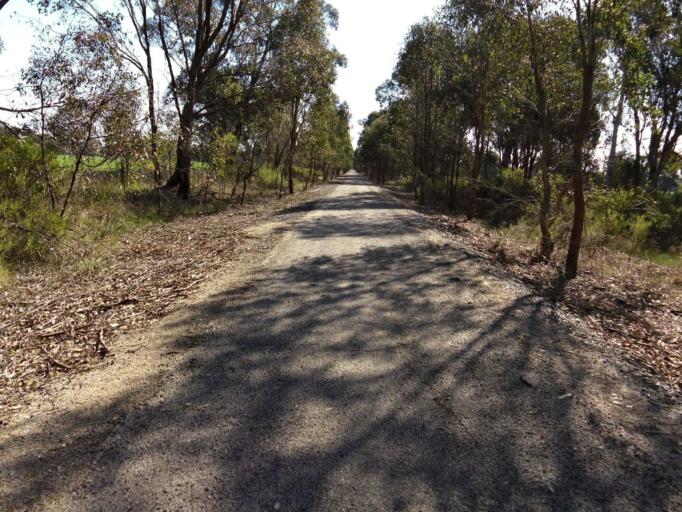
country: AU
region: New South Wales
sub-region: Corowa Shire
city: Corowa
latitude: -36.0296
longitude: 146.4389
